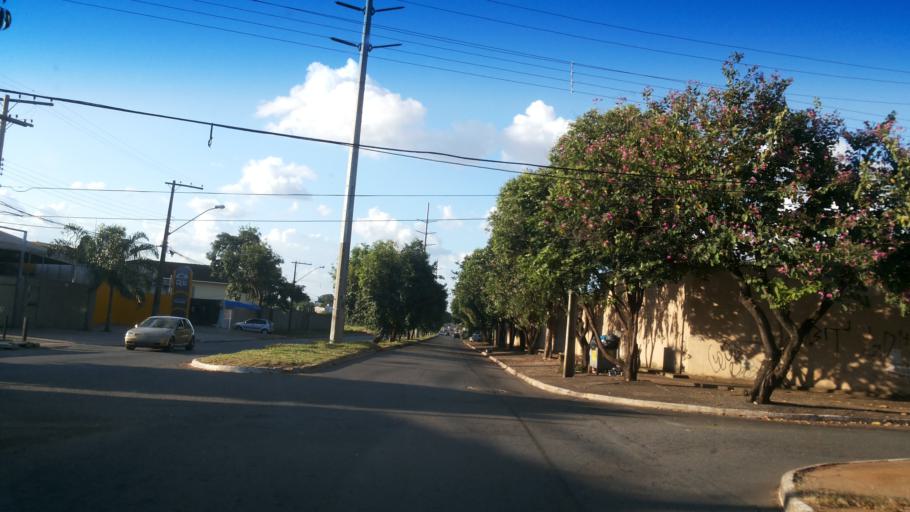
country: BR
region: Goias
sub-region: Goiania
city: Goiania
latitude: -16.7341
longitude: -49.3093
